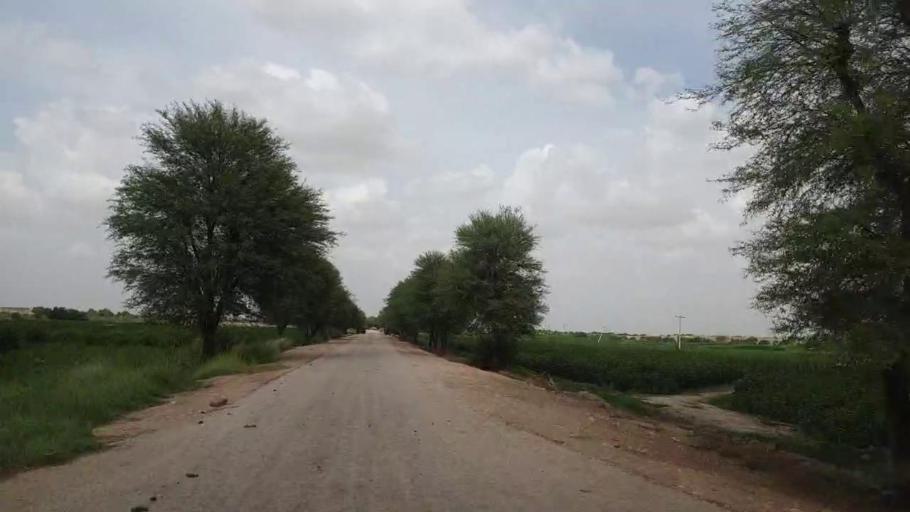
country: PK
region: Sindh
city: Kot Diji
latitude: 27.2251
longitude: 69.0866
